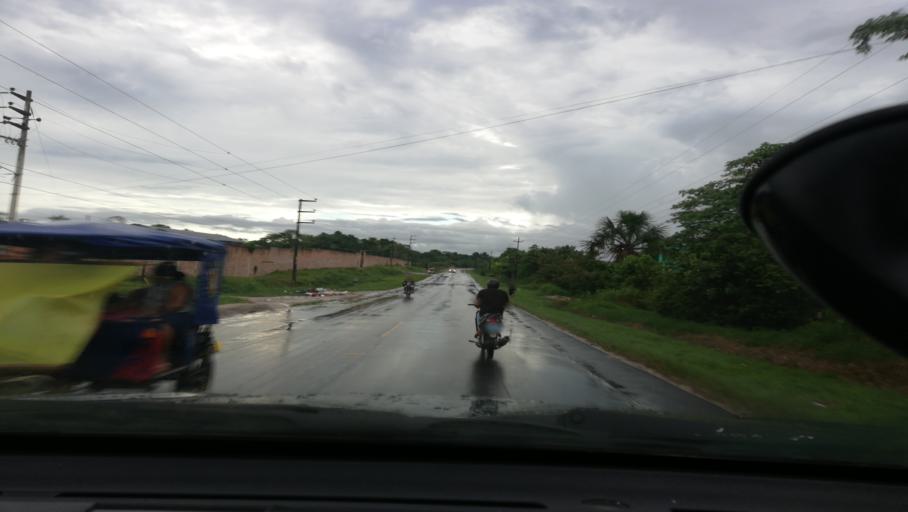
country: PE
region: Loreto
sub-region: Provincia de Maynas
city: Iquitos
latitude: -3.8377
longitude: -73.3294
